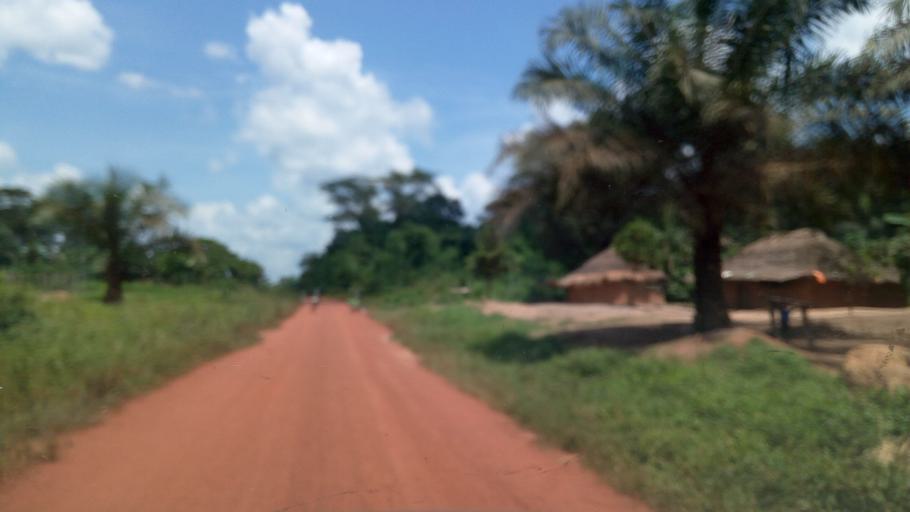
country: CD
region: Equateur
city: Gemena
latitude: 3.2949
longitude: 19.4957
